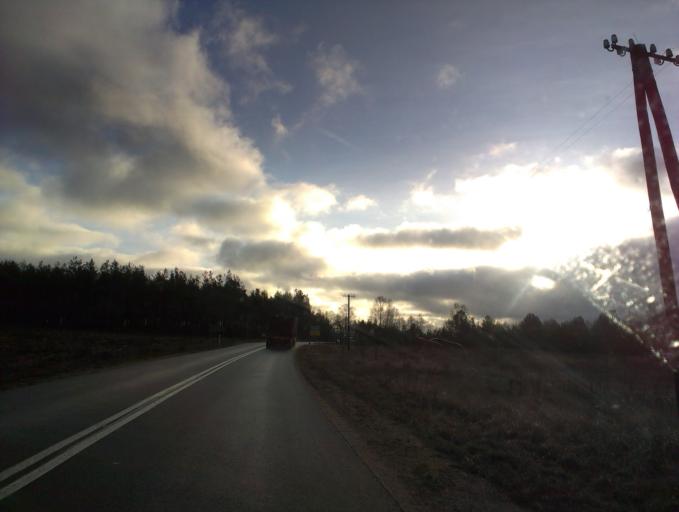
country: PL
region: Pomeranian Voivodeship
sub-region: Powiat czluchowski
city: Czarne
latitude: 53.6905
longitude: 16.9218
